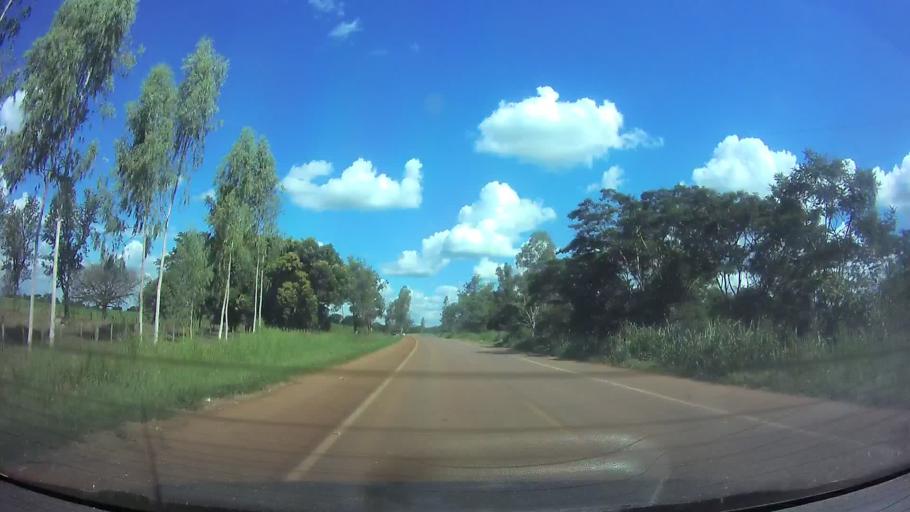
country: PY
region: Guaira
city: Coronel Martinez
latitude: -25.7875
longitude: -56.6471
